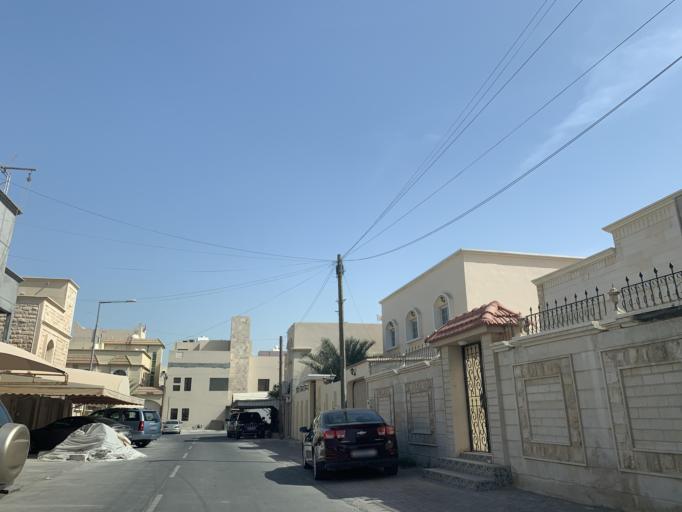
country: BH
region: Northern
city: Ar Rifa'
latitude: 26.1308
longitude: 50.5831
